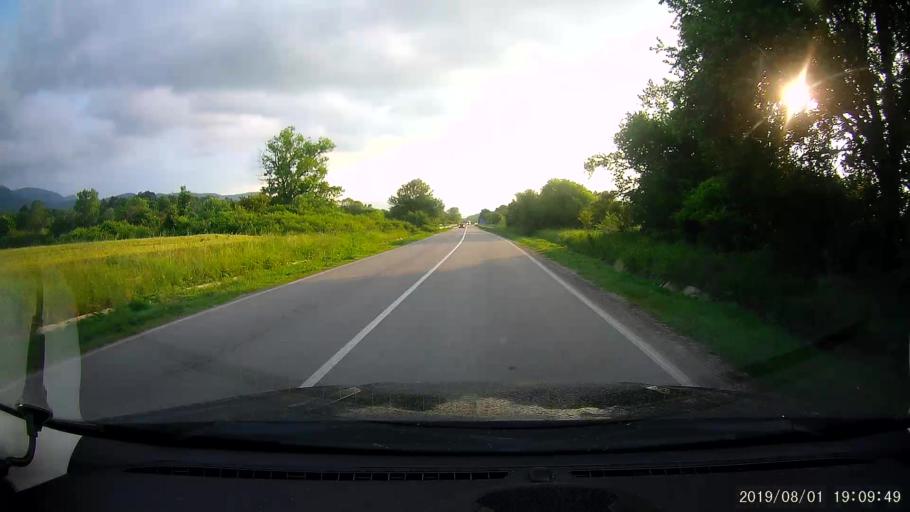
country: BG
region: Shumen
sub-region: Obshtina Smyadovo
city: Smyadovo
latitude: 42.9851
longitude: 26.9948
